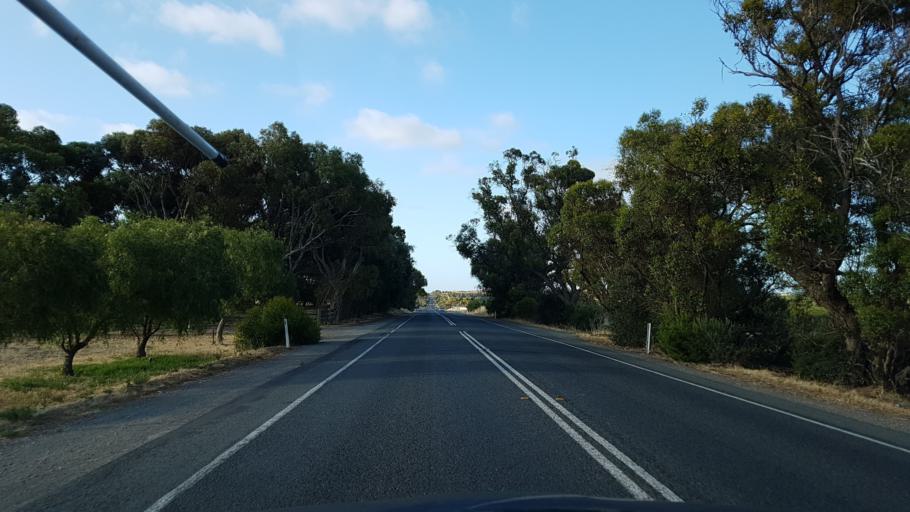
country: AU
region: South Australia
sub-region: Onkaparinga
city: Moana
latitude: -35.2369
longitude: 138.4938
